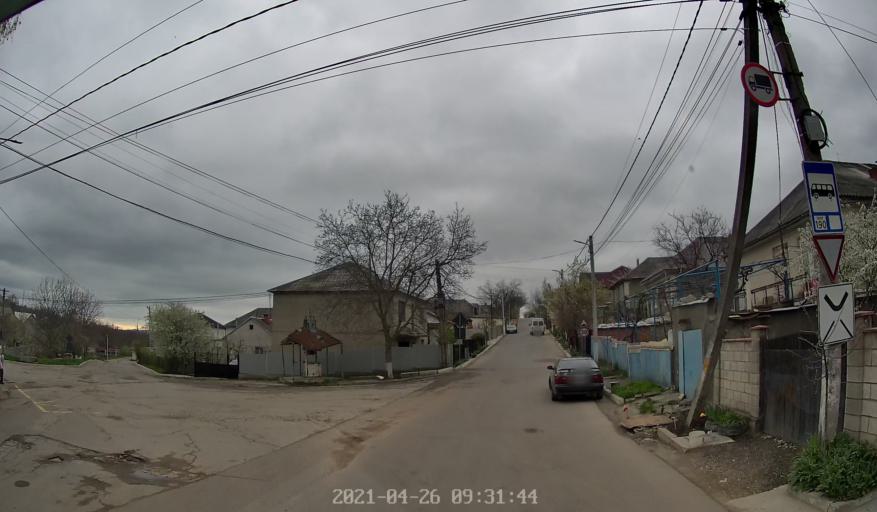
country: MD
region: Chisinau
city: Stauceni
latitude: 47.0943
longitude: 28.8694
